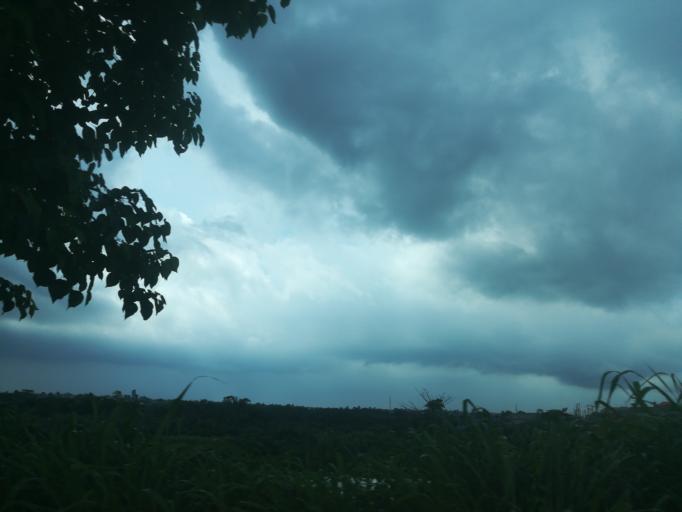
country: NG
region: Lagos
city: Ikorodu
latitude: 6.6609
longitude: 3.5898
